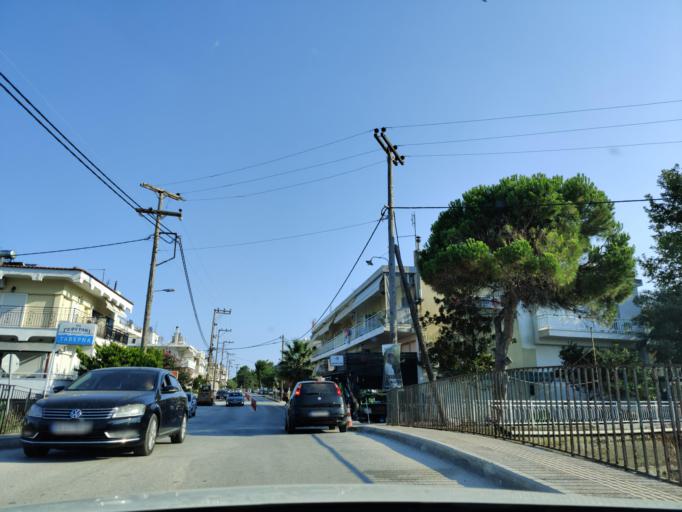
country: GR
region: East Macedonia and Thrace
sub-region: Nomos Kavalas
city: Nea Peramos
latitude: 40.8329
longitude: 24.3044
